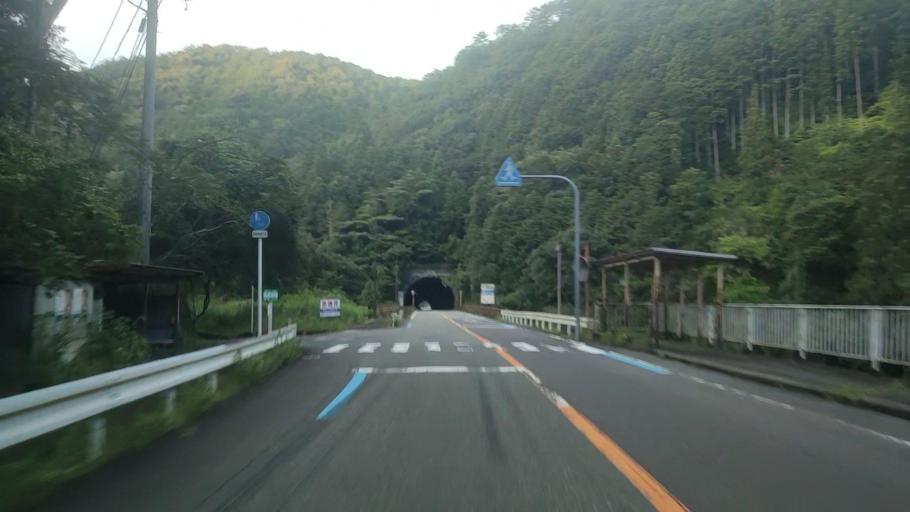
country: JP
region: Wakayama
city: Shingu
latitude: 33.8156
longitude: 135.7559
